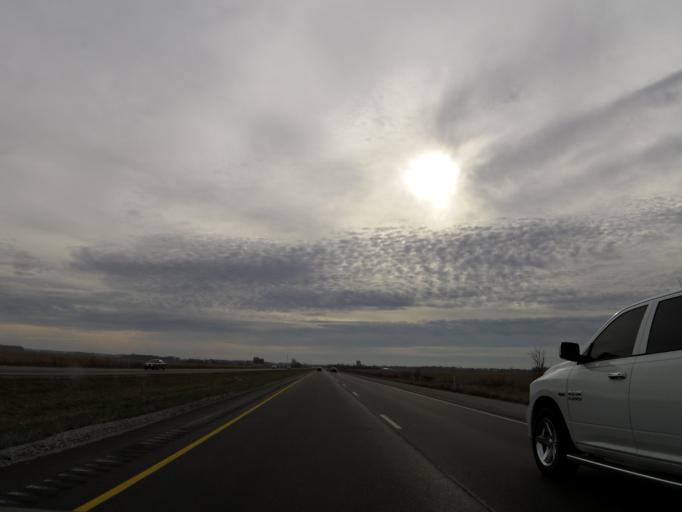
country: US
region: Indiana
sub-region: Montgomery County
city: Crawfordsville
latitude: 40.0395
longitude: -86.8028
